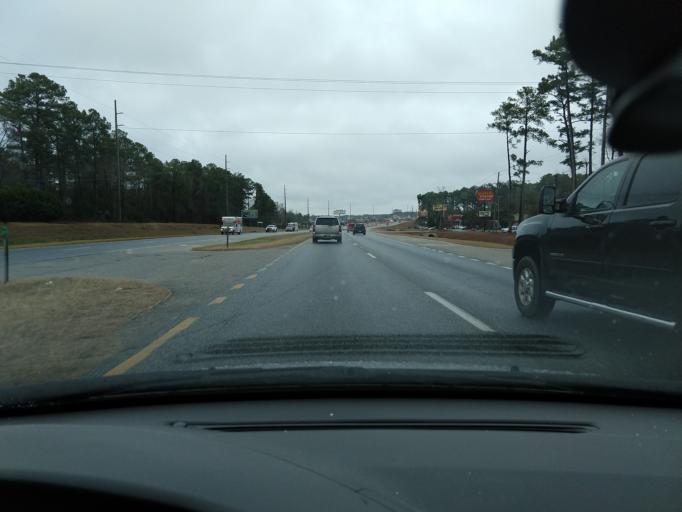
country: US
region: Alabama
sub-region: Houston County
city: Dothan
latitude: 31.2389
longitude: -85.4314
